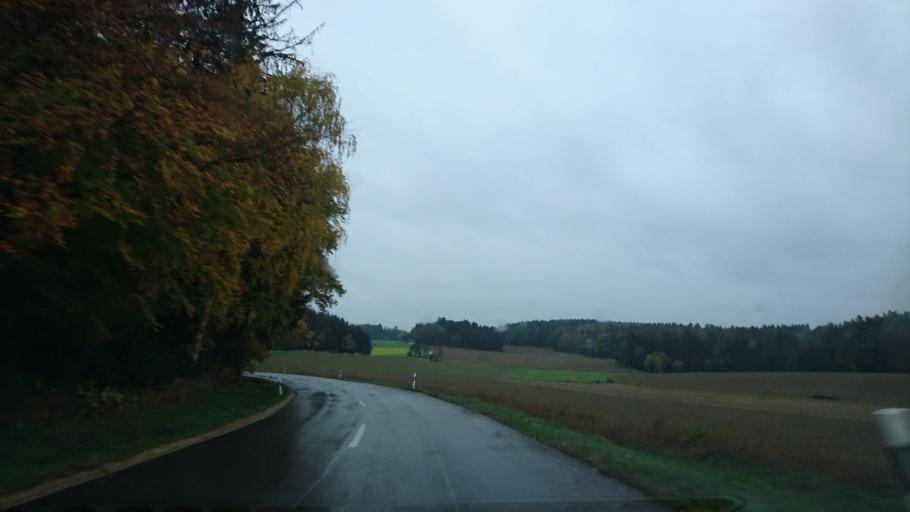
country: DE
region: Bavaria
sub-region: Swabia
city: Schiltberg
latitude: 48.4330
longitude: 11.2867
